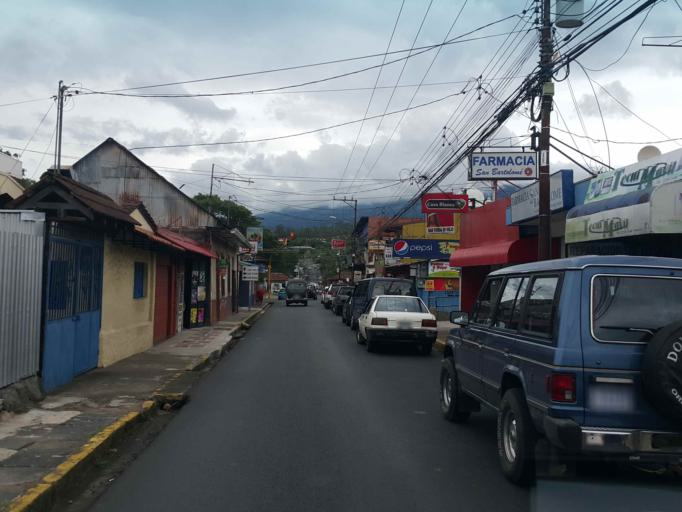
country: CR
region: Heredia
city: Mercedes
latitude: 10.0197
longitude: -84.1236
